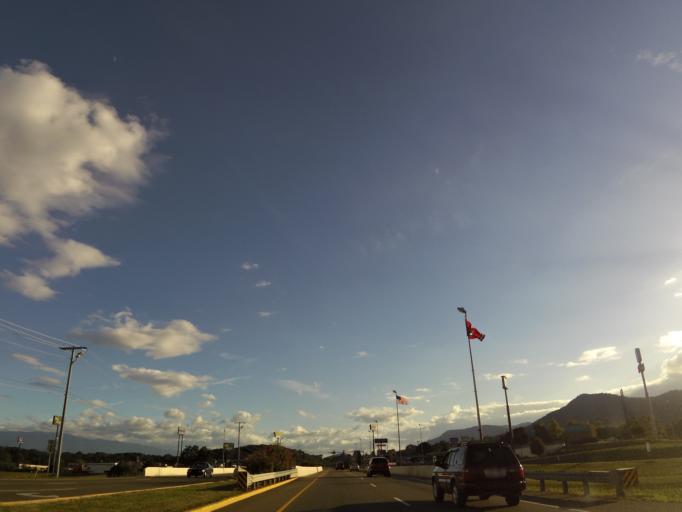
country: US
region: Tennessee
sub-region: Cocke County
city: Newport
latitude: 35.9489
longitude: -83.2027
